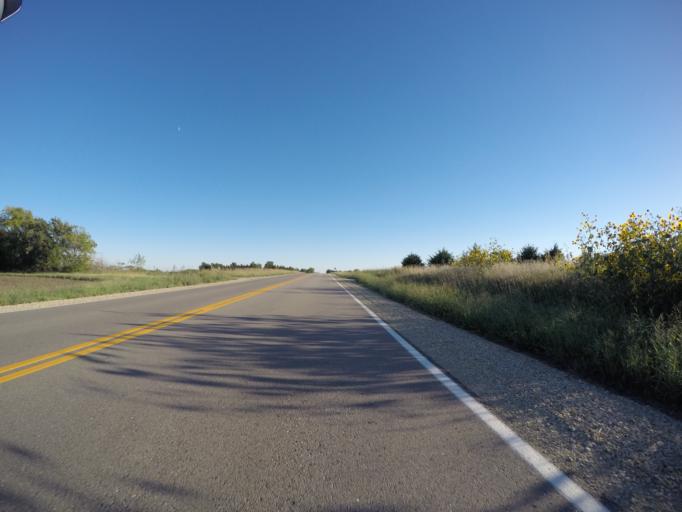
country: US
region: Kansas
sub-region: Riley County
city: Fort Riley North
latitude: 39.2916
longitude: -96.7750
